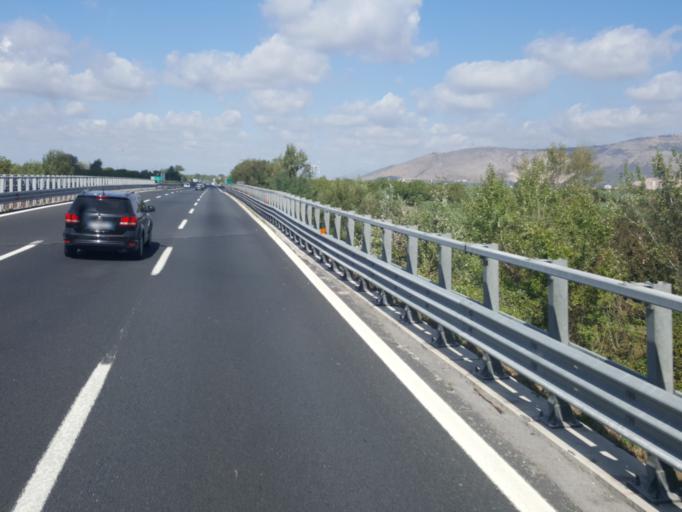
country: IT
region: Campania
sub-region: Provincia di Napoli
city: San Vitaliano
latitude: 40.9484
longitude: 14.4782
